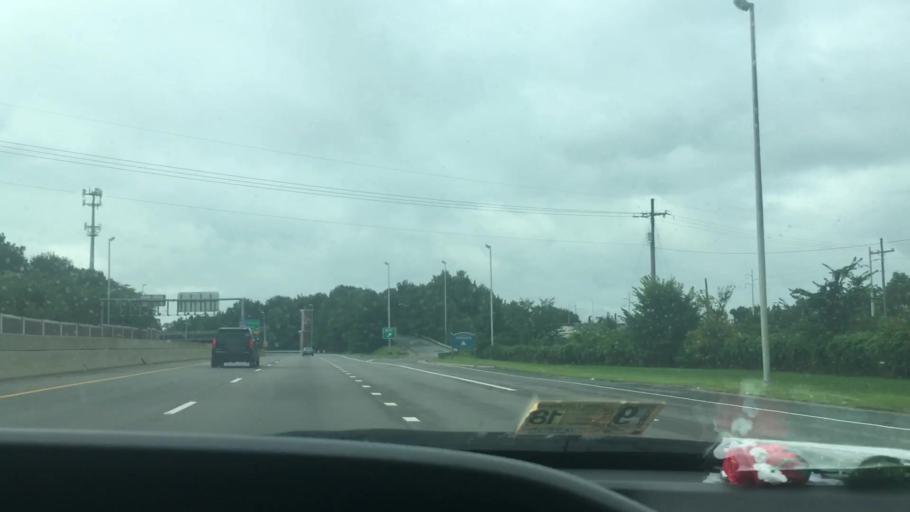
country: US
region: Virginia
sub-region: City of Portsmouth
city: Portsmouth
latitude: 36.8406
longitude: -76.3293
